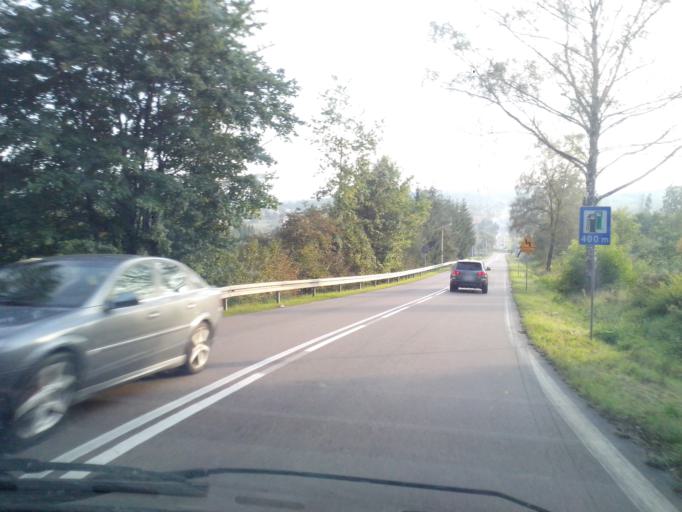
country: PL
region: Subcarpathian Voivodeship
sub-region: Powiat brzozowski
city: Domaradz
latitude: 49.7976
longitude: 21.9513
